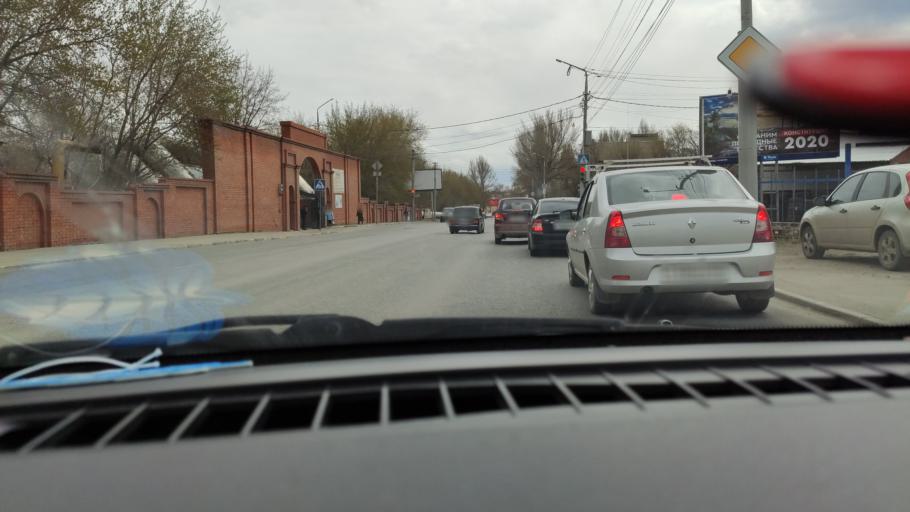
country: RU
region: Saratov
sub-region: Saratovskiy Rayon
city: Saratov
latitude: 51.5549
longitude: 46.0076
